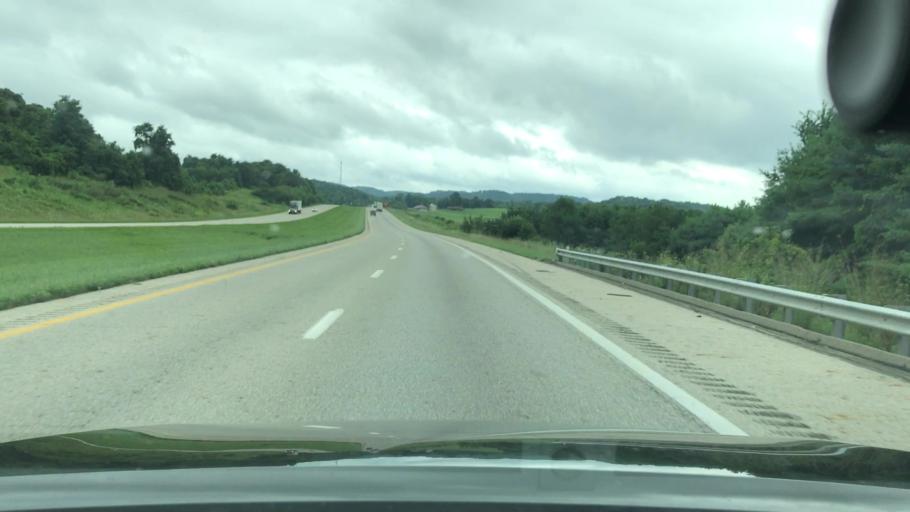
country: US
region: Ohio
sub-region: Ross County
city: Chillicothe
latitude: 39.2633
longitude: -82.8682
